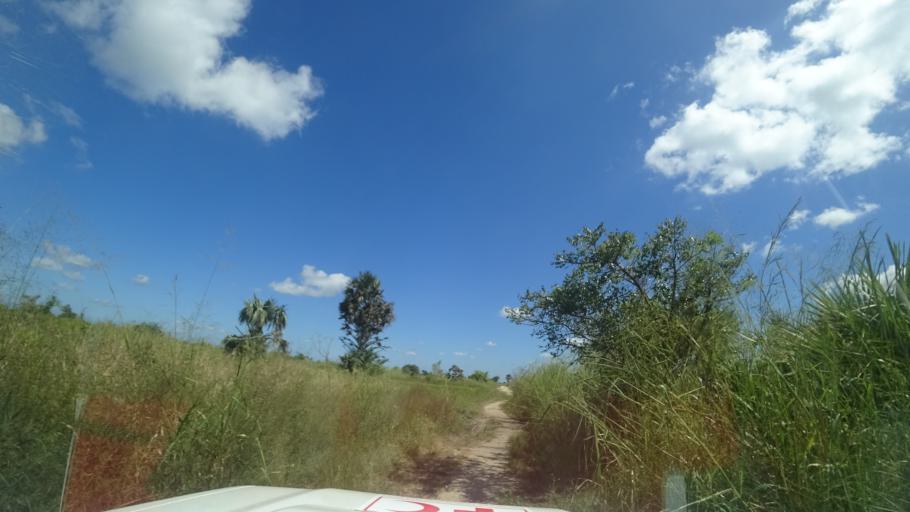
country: MZ
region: Sofala
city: Dondo
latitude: -19.3869
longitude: 34.5920
